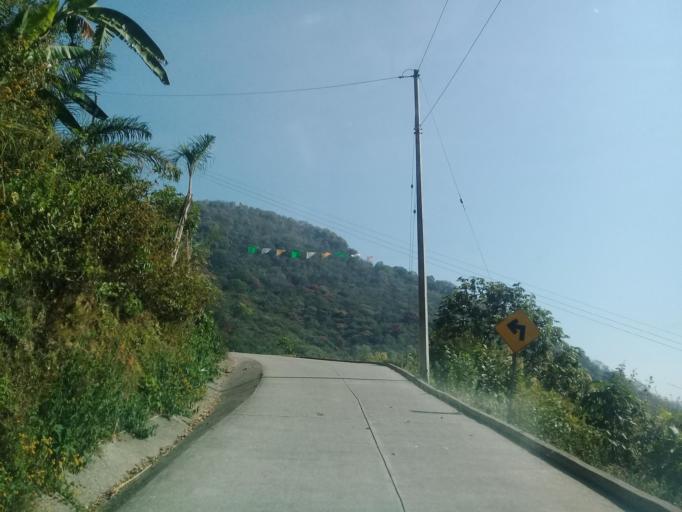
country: MX
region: Veracruz
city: Rafael Delgado
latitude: 18.7823
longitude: -97.0271
